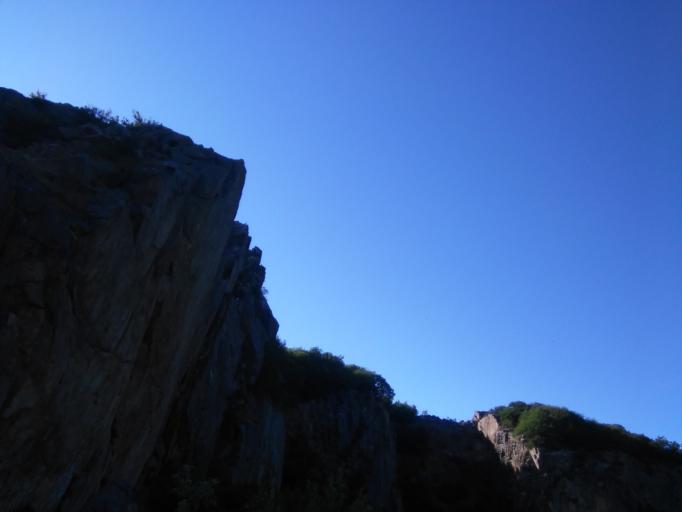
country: DK
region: Capital Region
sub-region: Bornholm Kommune
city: Ronne
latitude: 55.2818
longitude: 14.7608
